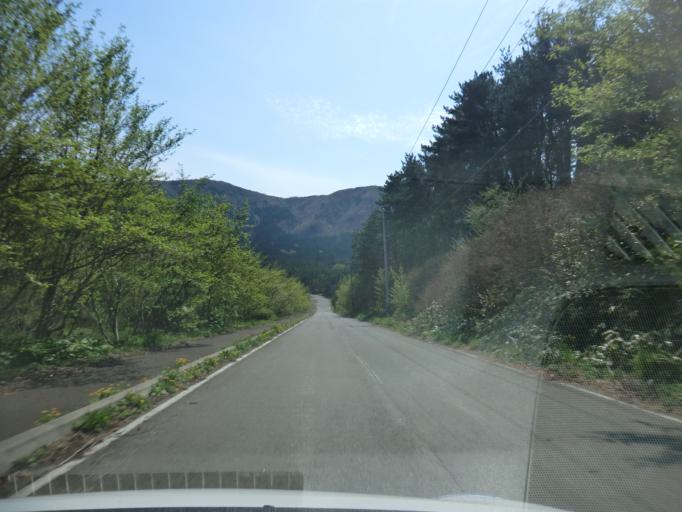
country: JP
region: Aomori
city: Mutsu
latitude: 41.4039
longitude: 141.4564
